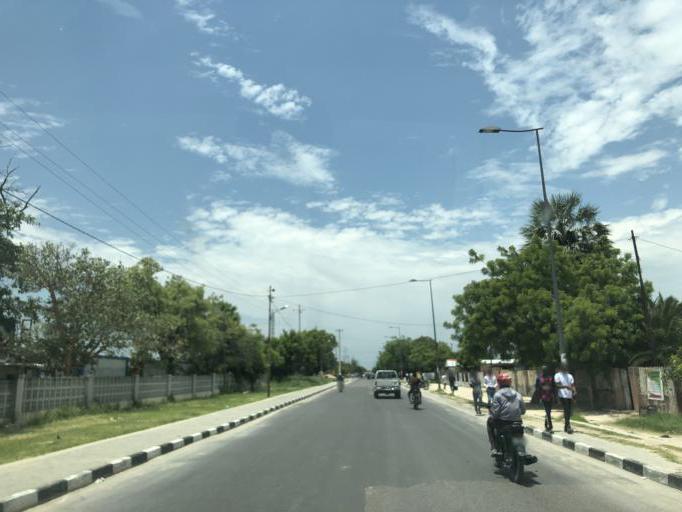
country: AO
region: Cunene
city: Ondjiva
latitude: -17.0697
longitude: 15.7239
